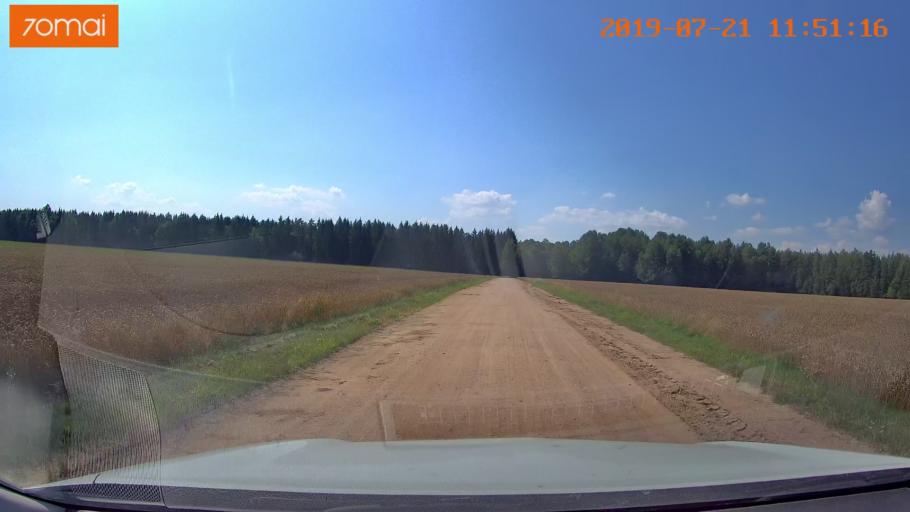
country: BY
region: Grodnenskaya
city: Lyubcha
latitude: 53.8847
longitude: 26.0138
